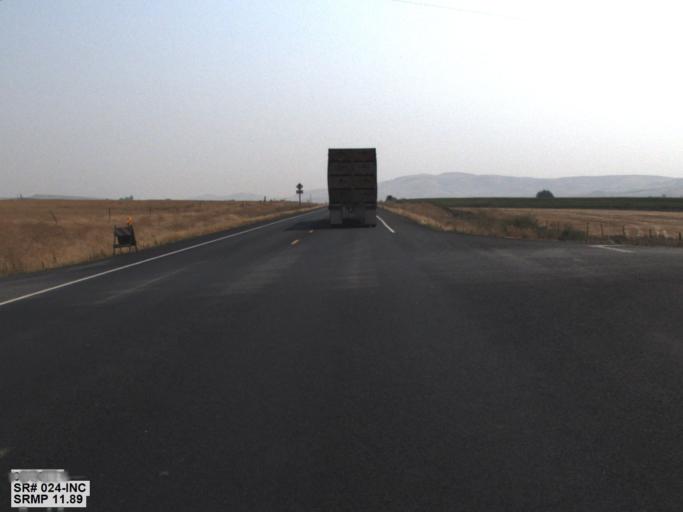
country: US
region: Washington
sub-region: Yakima County
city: Zillah
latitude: 46.5249
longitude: -120.2506
